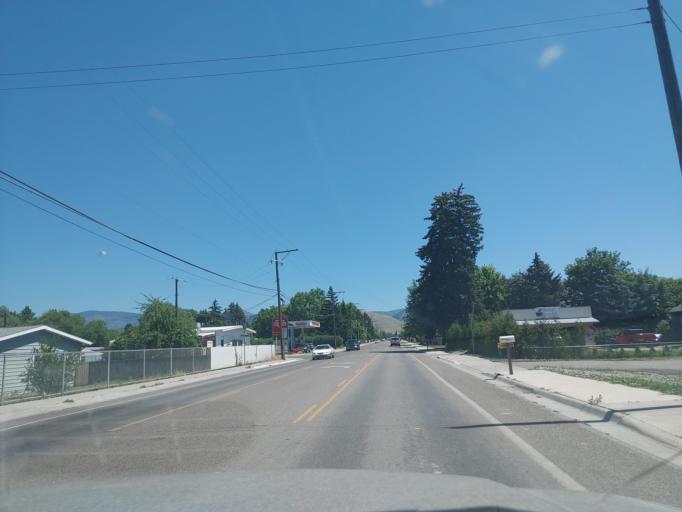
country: US
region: Montana
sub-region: Missoula County
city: Orchard Homes
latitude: 46.8669
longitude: -114.0379
